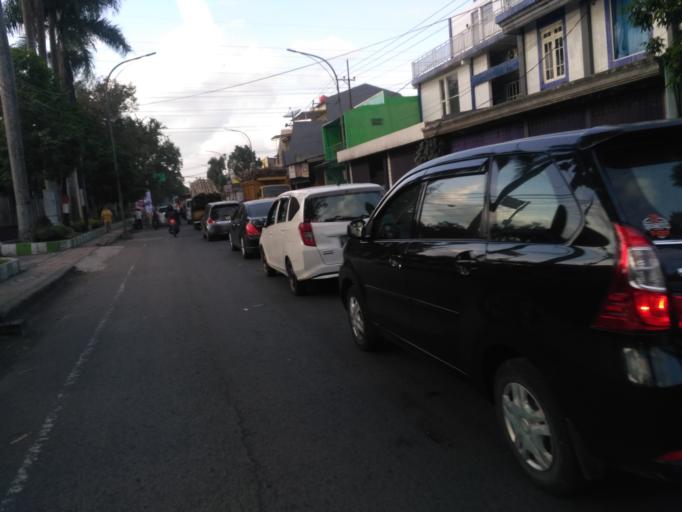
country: ID
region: East Java
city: Kebonsari
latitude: -8.0228
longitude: 112.6179
